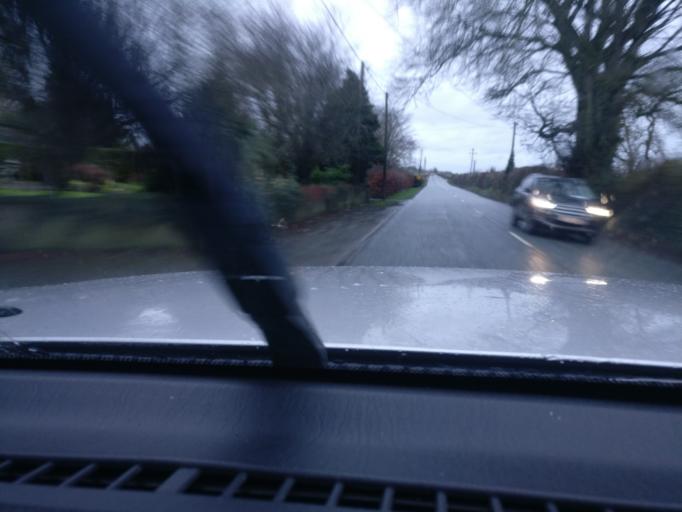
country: IE
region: Leinster
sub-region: An Mhi
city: Trim
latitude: 53.5124
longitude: -6.8413
